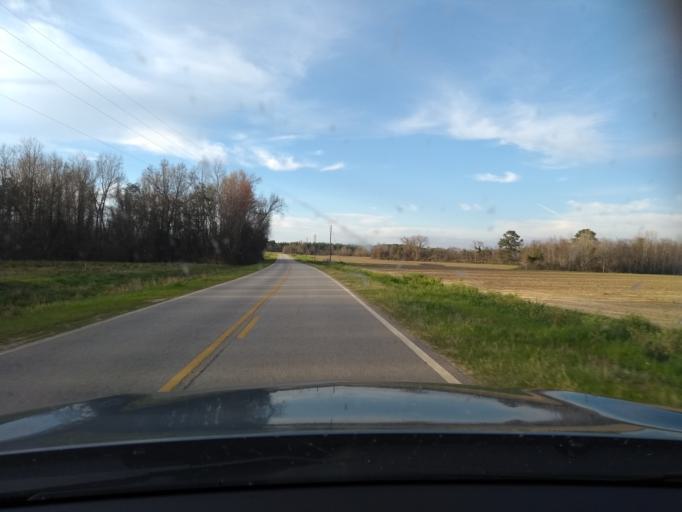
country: US
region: Georgia
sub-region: Bulloch County
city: Brooklet
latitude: 32.3033
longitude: -81.7734
